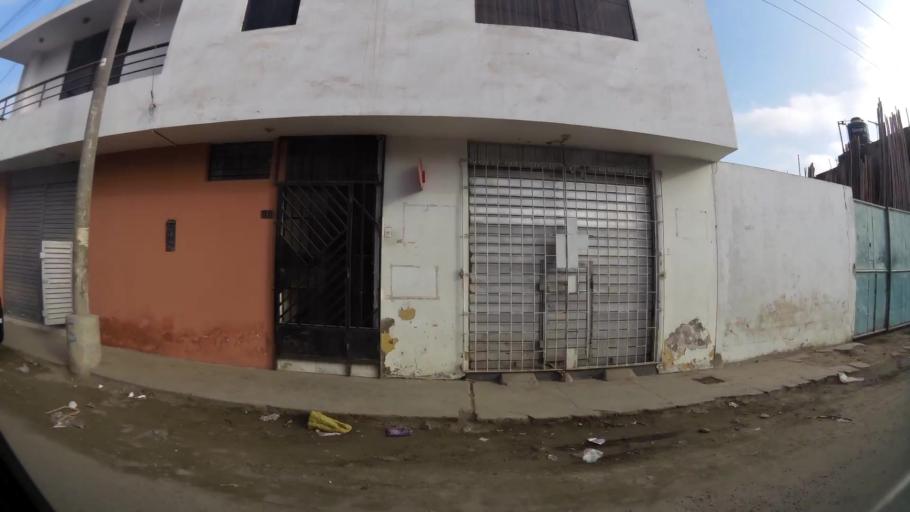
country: PE
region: La Libertad
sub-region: Provincia de Trujillo
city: El Porvenir
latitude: -8.0854
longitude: -79.0140
